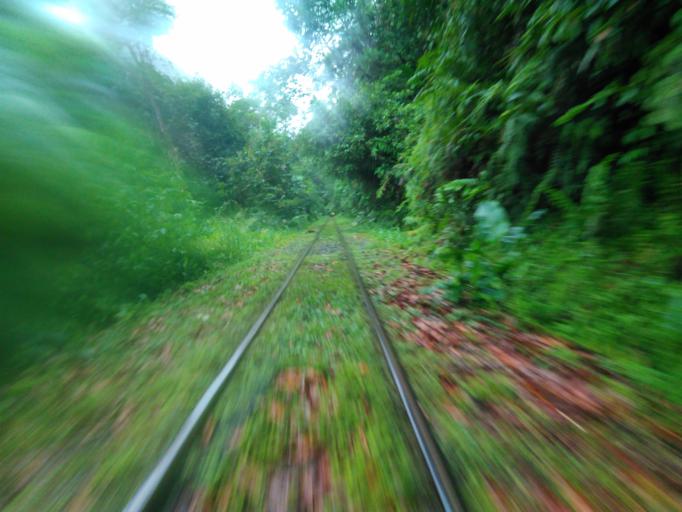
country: CO
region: Valle del Cauca
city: Buenaventura
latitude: 3.8481
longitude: -76.8837
